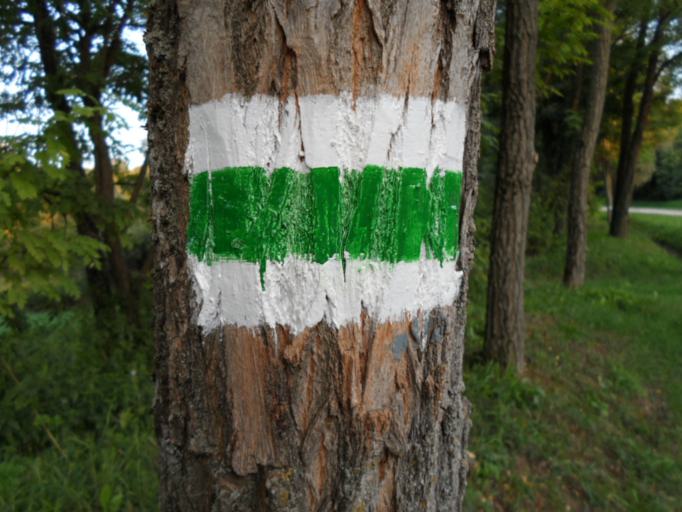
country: HU
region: Somogy
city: Marcali
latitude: 46.5122
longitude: 17.3912
